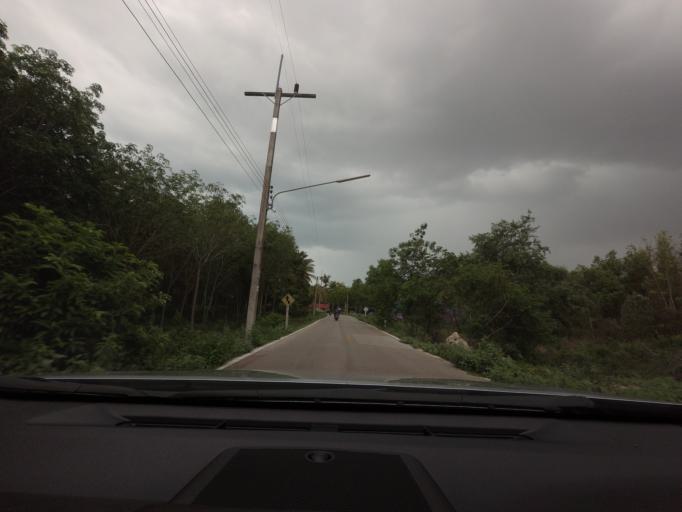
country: TH
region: Songkhla
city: Chana
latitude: 6.9538
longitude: 100.8394
